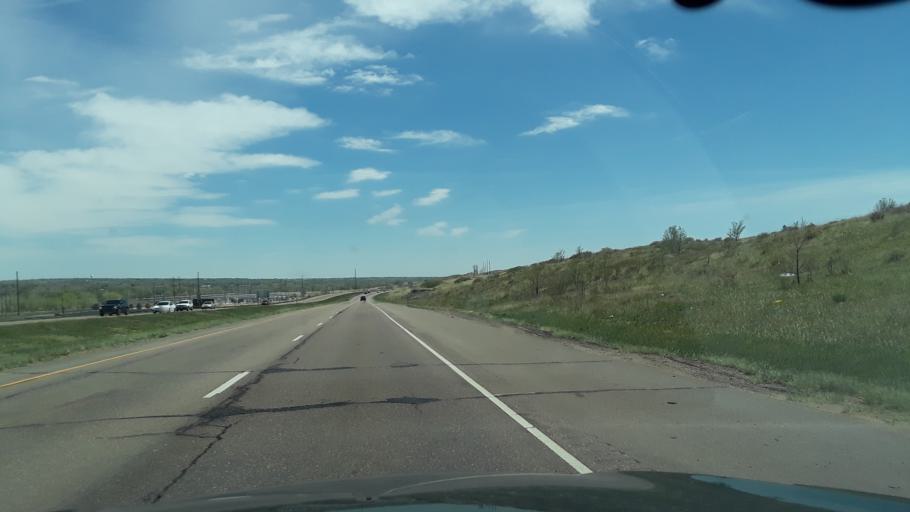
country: US
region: Colorado
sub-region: El Paso County
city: Stratmoor
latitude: 38.7594
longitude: -104.7693
